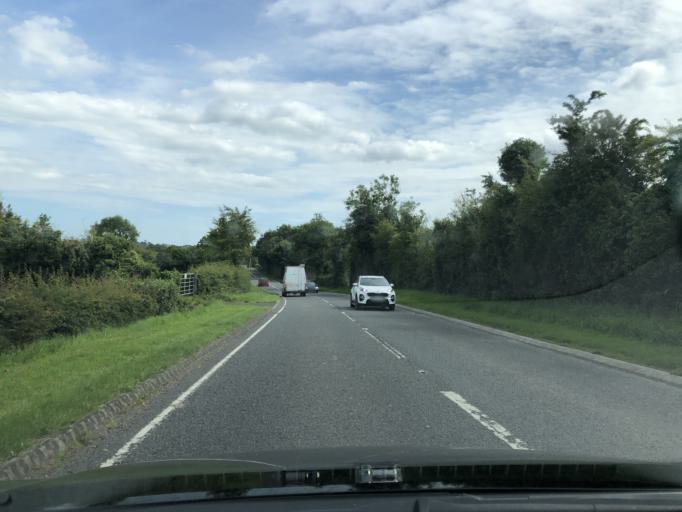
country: GB
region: Northern Ireland
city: Ballynahinch
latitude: 54.4241
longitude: -5.9212
